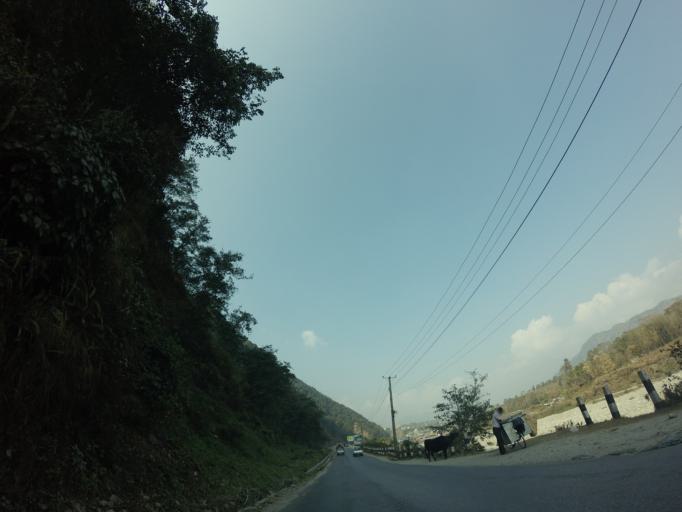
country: NP
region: Western Region
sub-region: Gandaki Zone
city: Pokhara
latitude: 28.2504
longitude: 83.9716
